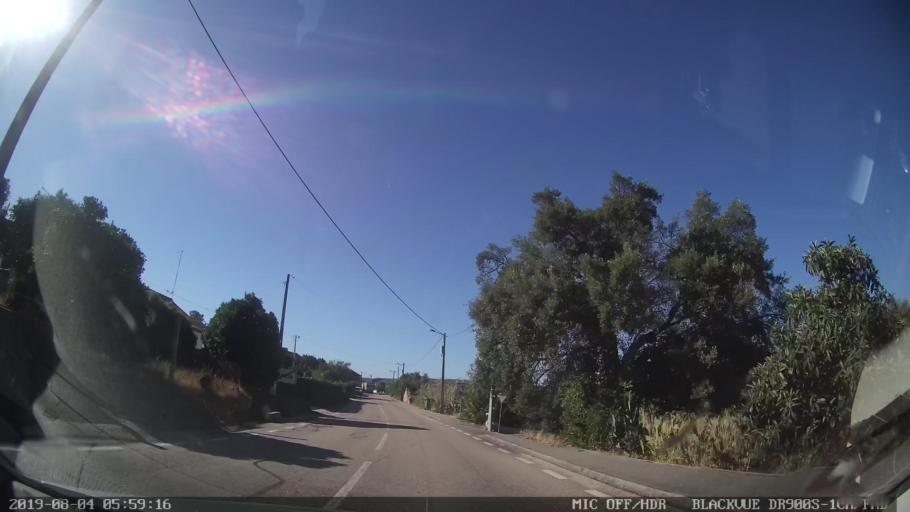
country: PT
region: Portalegre
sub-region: Gaviao
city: Gaviao
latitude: 39.4588
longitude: -8.0099
